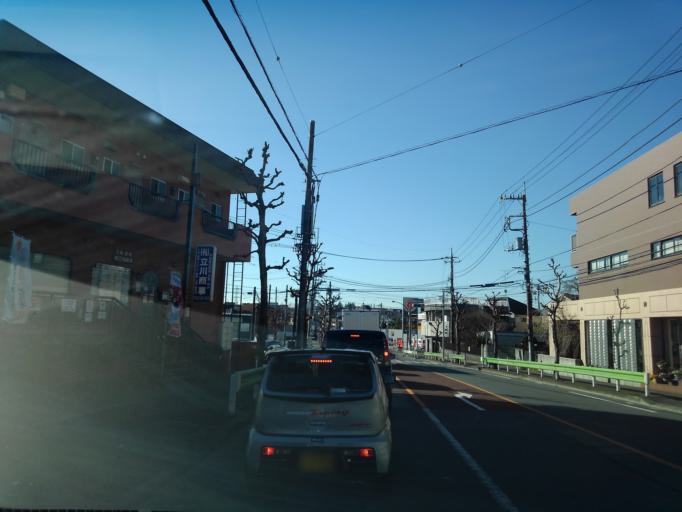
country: JP
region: Tokyo
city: Hino
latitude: 35.6818
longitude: 139.3675
